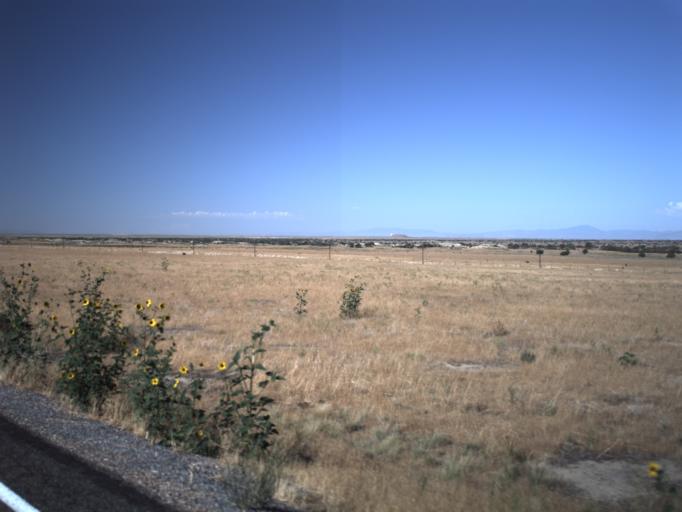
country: US
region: Utah
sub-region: Millard County
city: Delta
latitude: 39.6171
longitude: -112.3165
